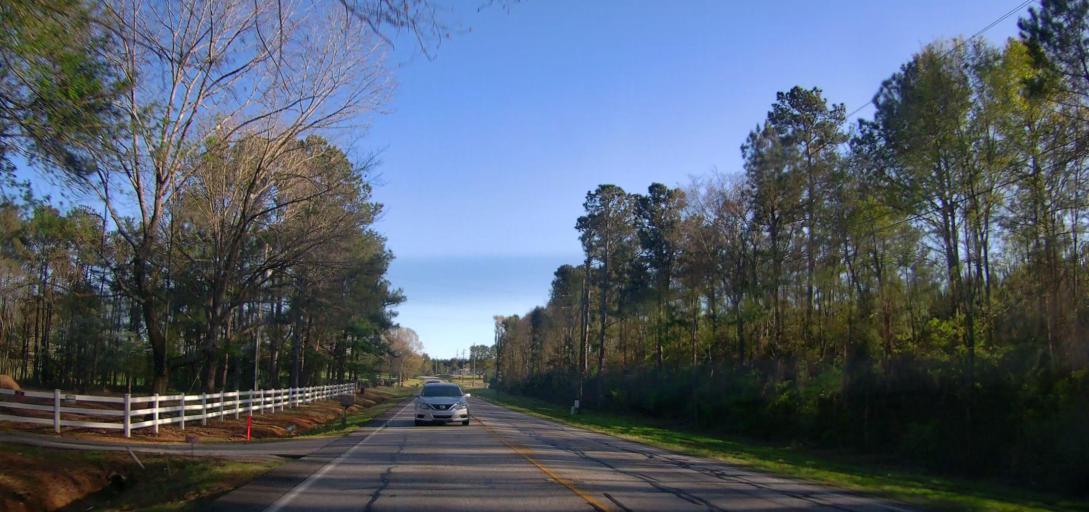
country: US
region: Georgia
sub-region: Newton County
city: Oakwood
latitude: 33.4455
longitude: -83.9027
